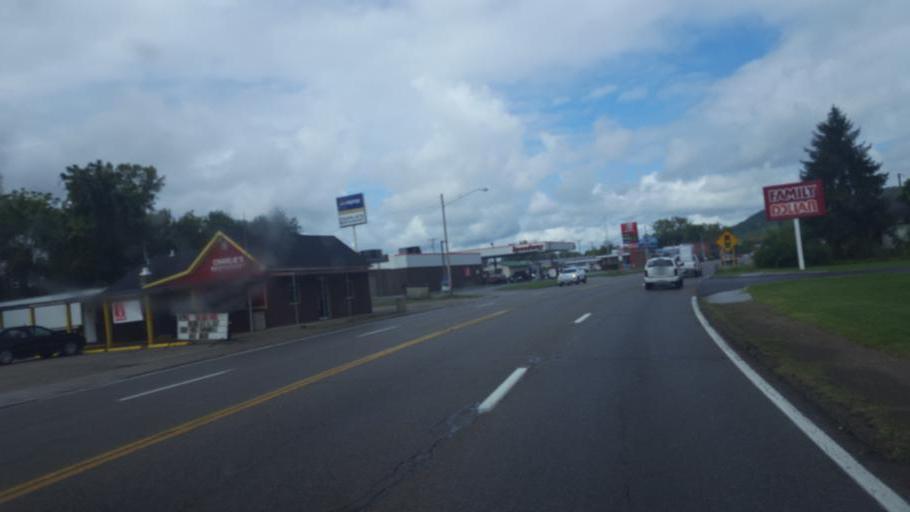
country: US
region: Ohio
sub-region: Scioto County
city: Lucasville
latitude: 38.8773
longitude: -82.9968
